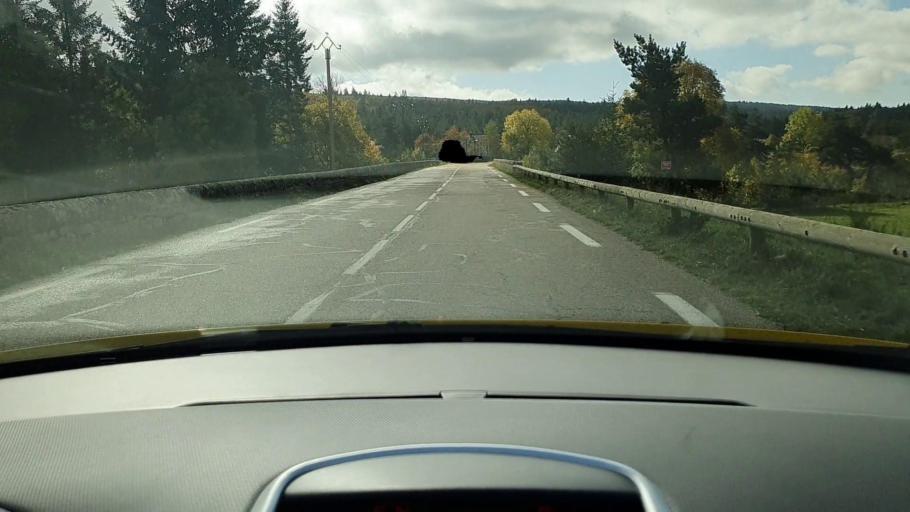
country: FR
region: Languedoc-Roussillon
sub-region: Departement de la Lozere
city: Meyrueis
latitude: 44.1166
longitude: 3.4862
